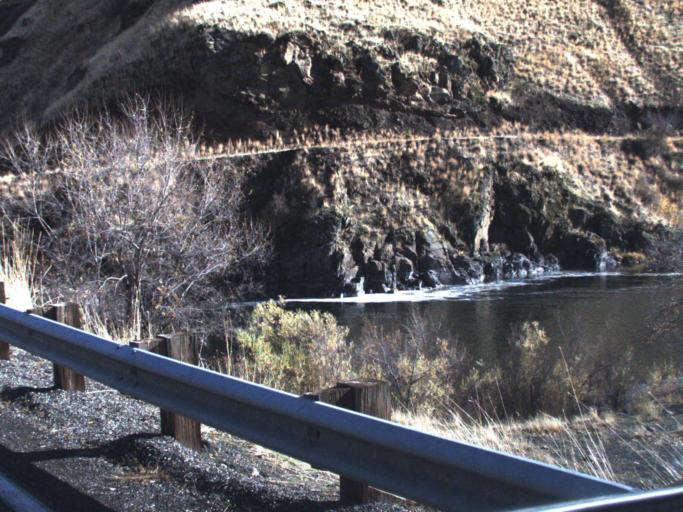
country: US
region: Washington
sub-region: Asotin County
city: Asotin
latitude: 46.0413
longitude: -117.2534
